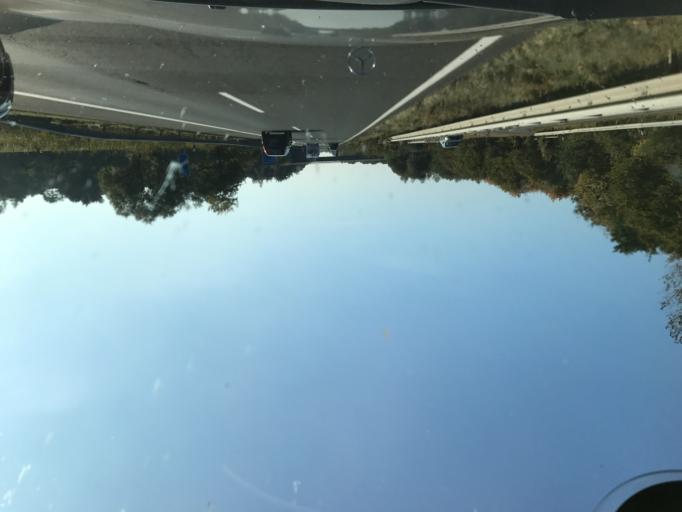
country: DE
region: Lower Saxony
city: Wiefelstede
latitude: 53.1918
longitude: 8.1010
